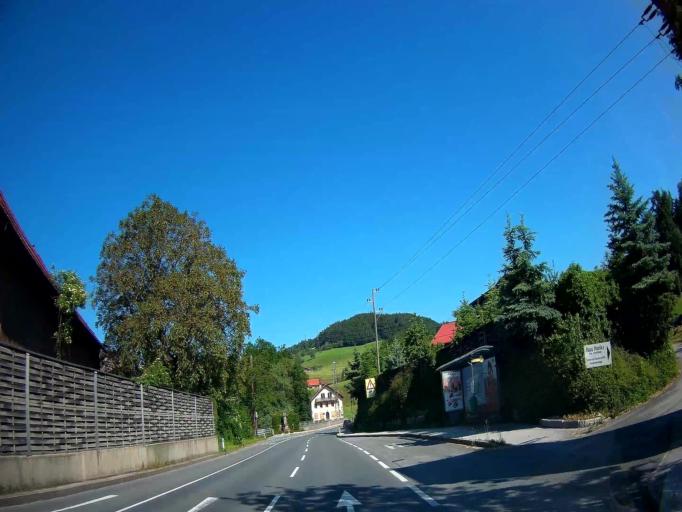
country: AT
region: Salzburg
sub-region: Politischer Bezirk Salzburg-Umgebung
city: Bergheim
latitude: 47.8467
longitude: 13.0471
